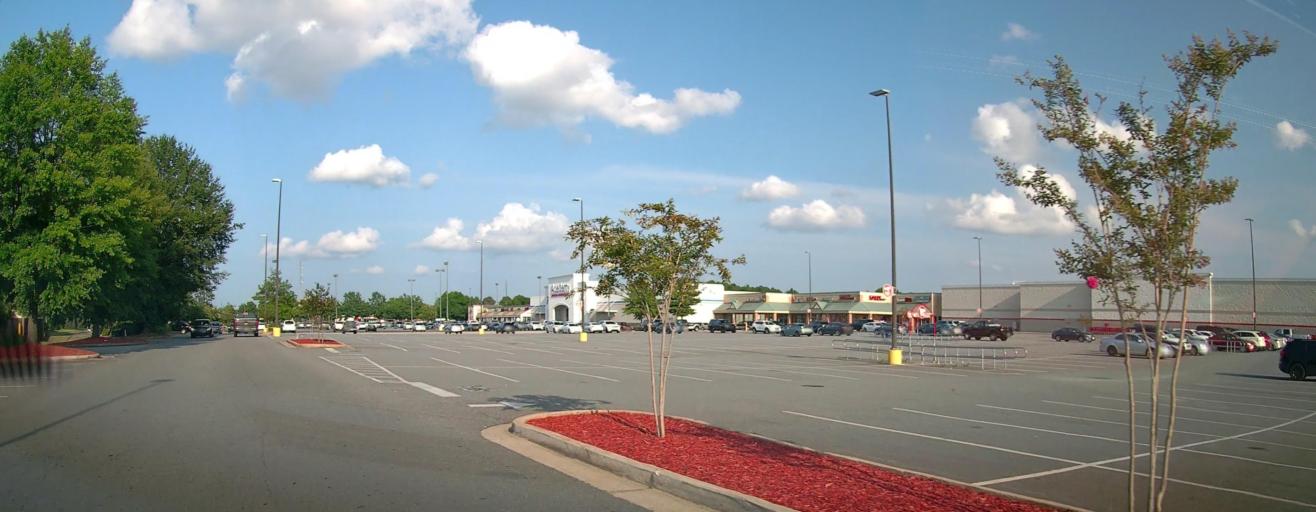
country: US
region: Georgia
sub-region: Houston County
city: Centerville
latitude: 32.6174
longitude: -83.6856
